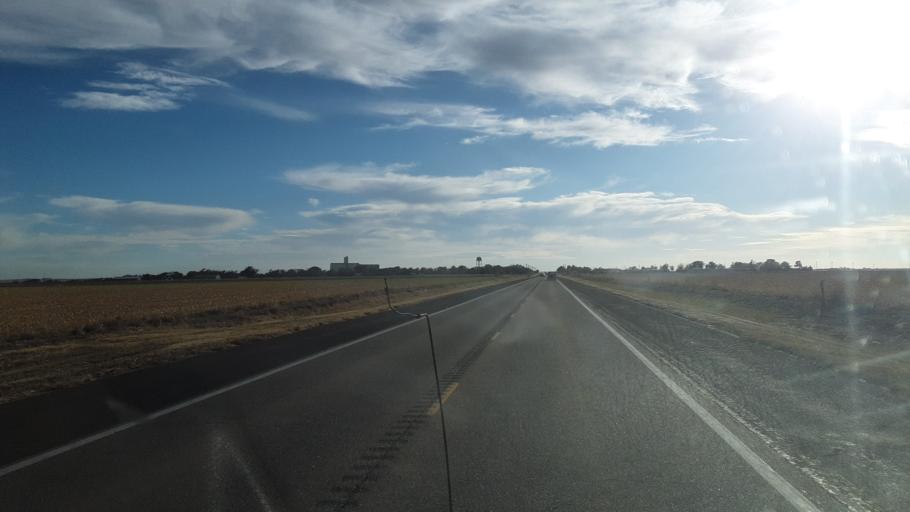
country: US
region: Kansas
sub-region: Kearny County
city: Lakin
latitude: 37.9935
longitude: -101.1301
